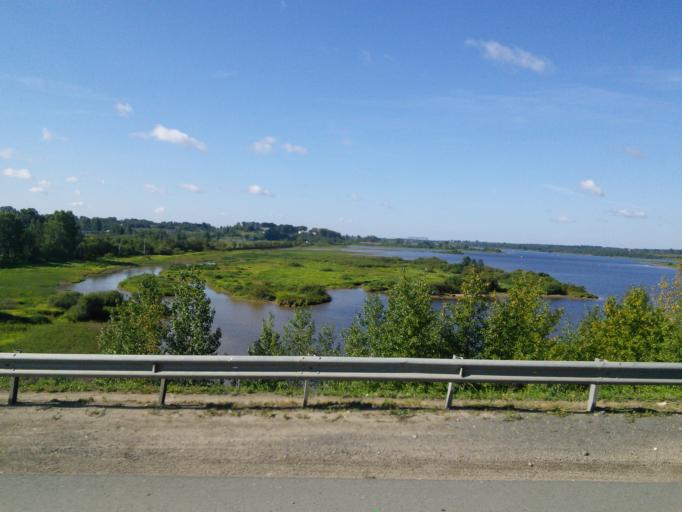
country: RU
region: Vologda
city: Sheksna
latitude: 59.2115
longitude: 38.4967
